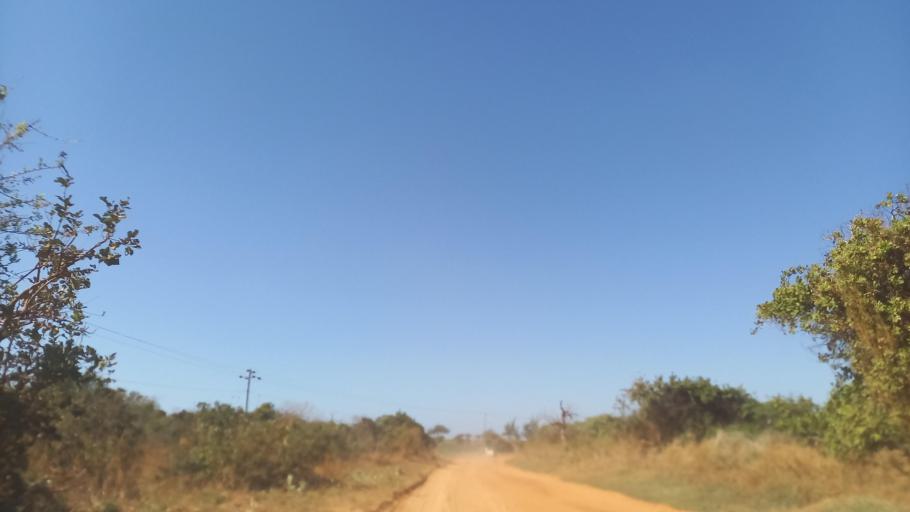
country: MZ
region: Cabo Delgado
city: Pemba
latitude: -13.1592
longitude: 40.5588
